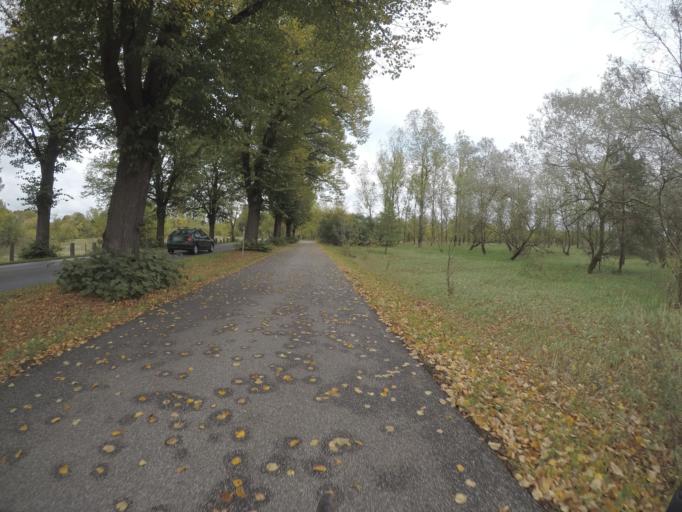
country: DE
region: Berlin
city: Buch
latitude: 52.6606
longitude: 13.4919
